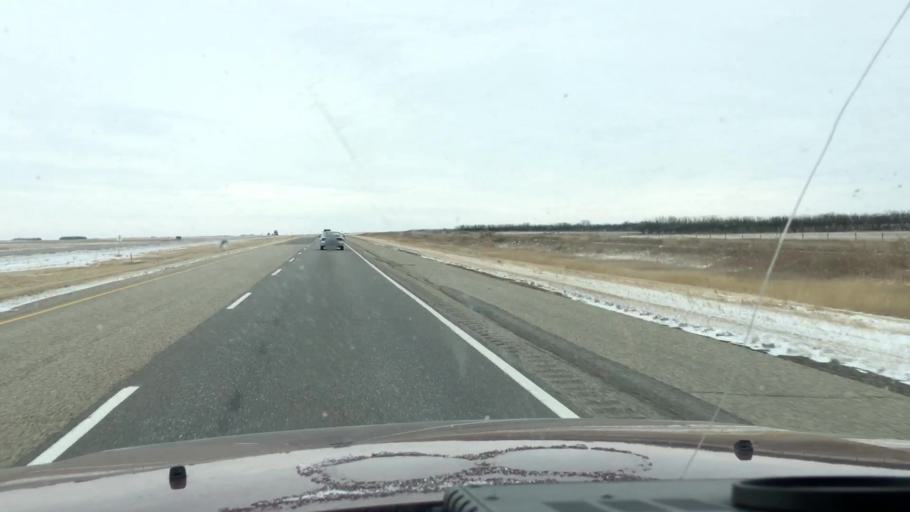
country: CA
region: Saskatchewan
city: Saskatoon
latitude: 51.4690
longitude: -106.2452
